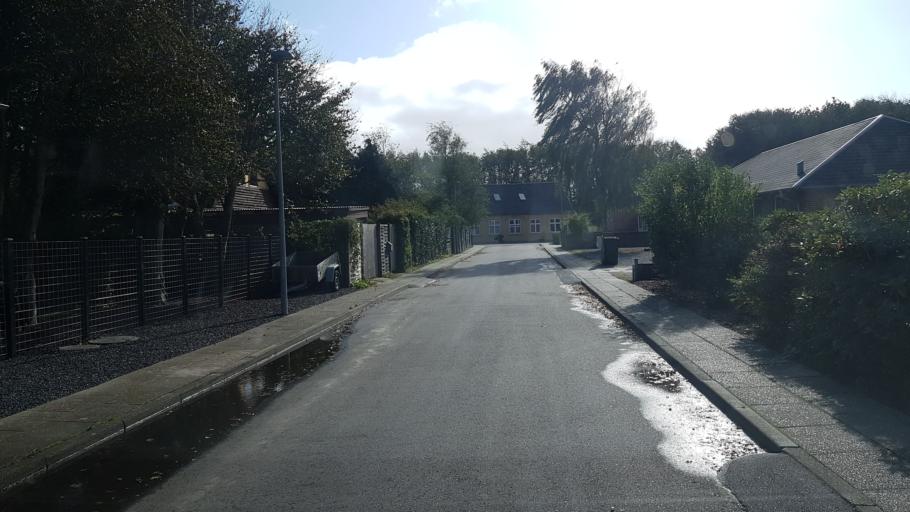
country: DK
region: South Denmark
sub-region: Varde Kommune
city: Olgod
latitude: 55.7158
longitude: 8.6005
